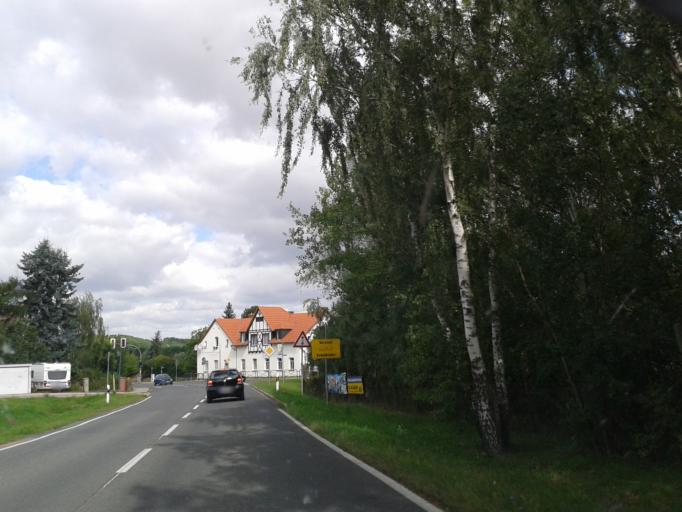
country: DE
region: Saxony-Anhalt
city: Salzmunde
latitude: 51.5256
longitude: 11.8361
